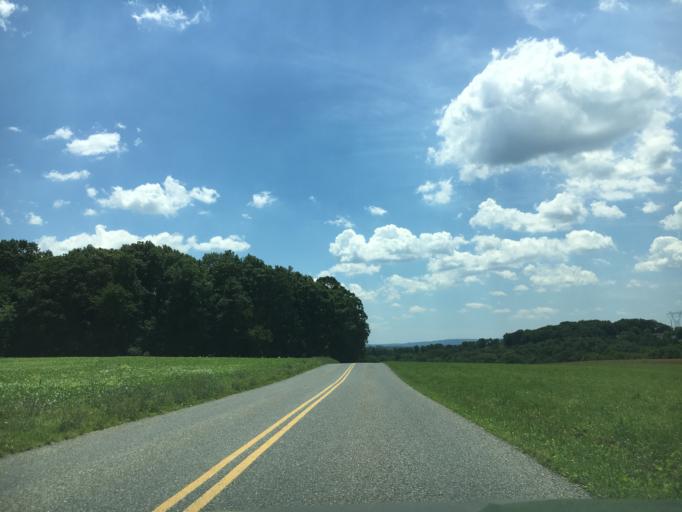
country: US
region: Pennsylvania
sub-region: Lehigh County
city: Schnecksville
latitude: 40.6756
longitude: -75.5802
